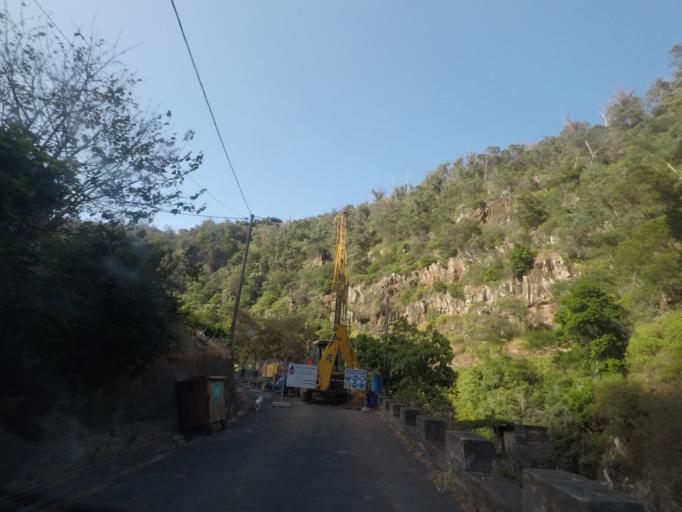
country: PT
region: Madeira
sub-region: Santa Cruz
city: Santa Cruz
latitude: 32.6946
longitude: -16.8054
